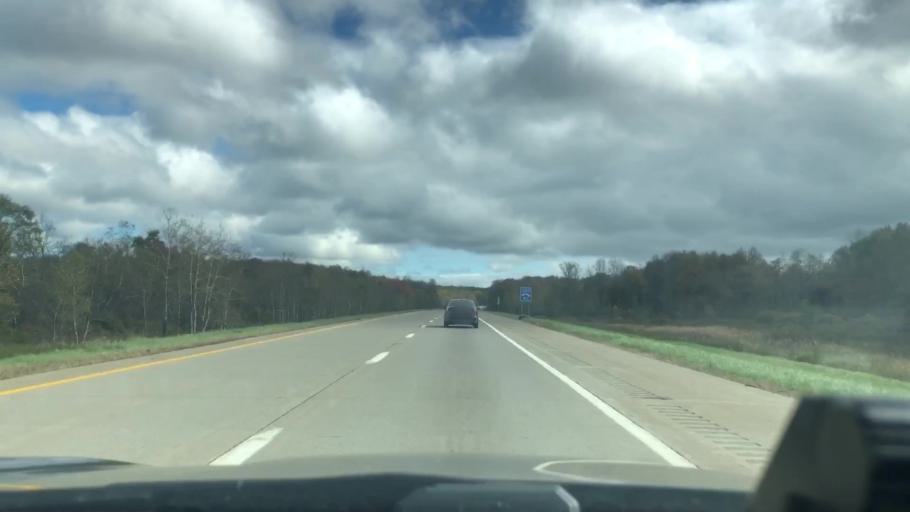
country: US
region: Pennsylvania
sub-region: Lackawanna County
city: Moscow
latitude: 41.2244
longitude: -75.4886
